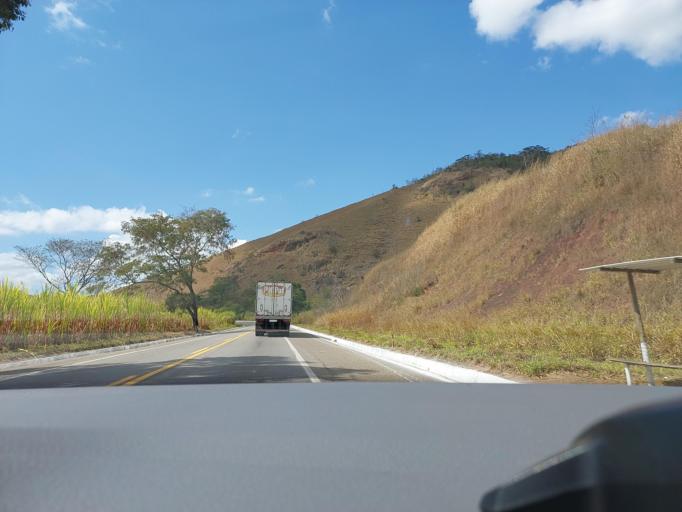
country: BR
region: Minas Gerais
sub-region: Muriae
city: Muriae
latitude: -21.1266
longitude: -42.2361
